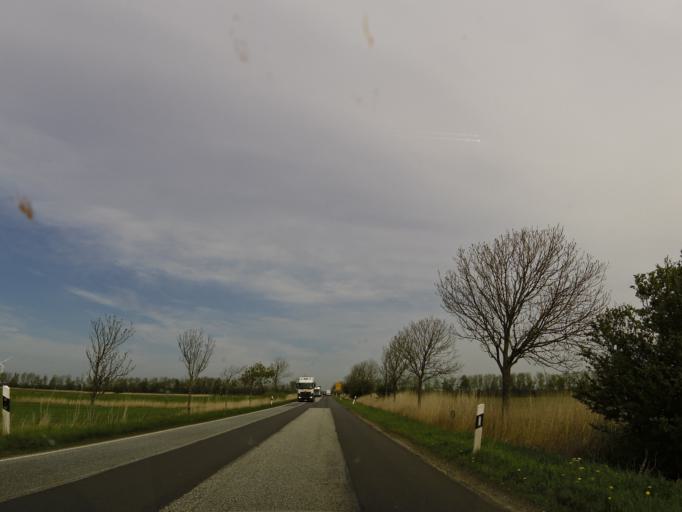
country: DE
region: Schleswig-Holstein
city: Husum
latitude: 54.4450
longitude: 9.0468
